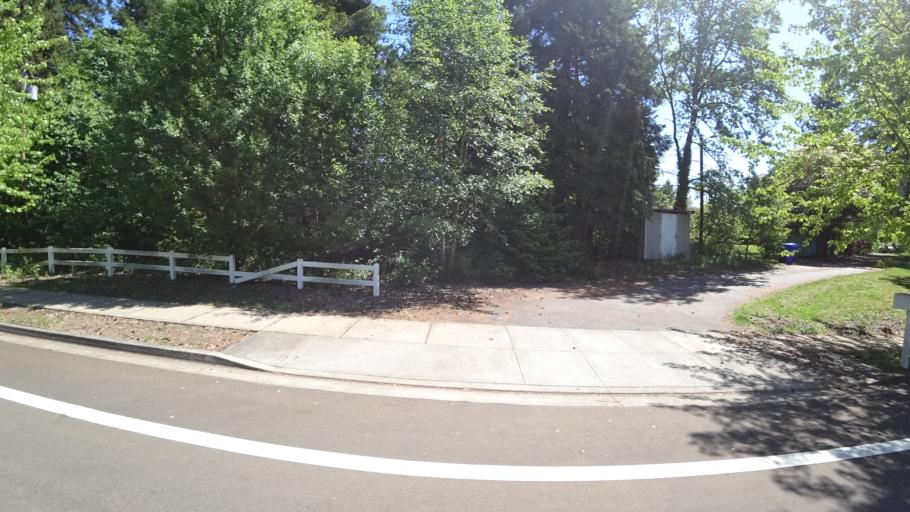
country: US
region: Oregon
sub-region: Washington County
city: Rockcreek
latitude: 45.5207
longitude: -122.9109
